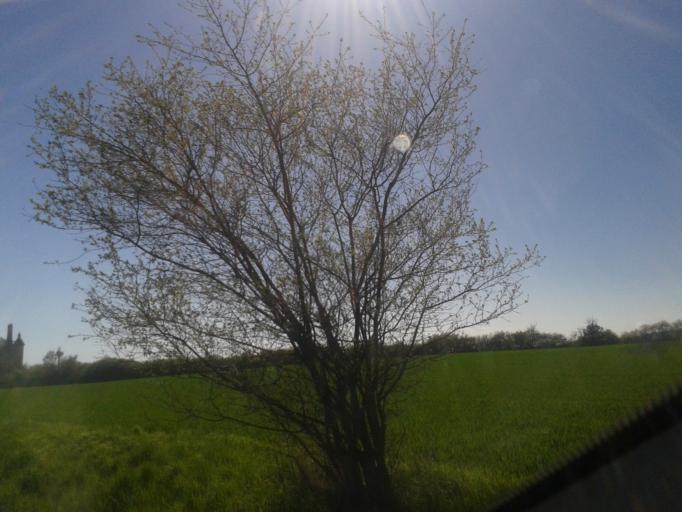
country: CZ
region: Central Bohemia
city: Revnice
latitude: 49.8808
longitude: 14.1473
